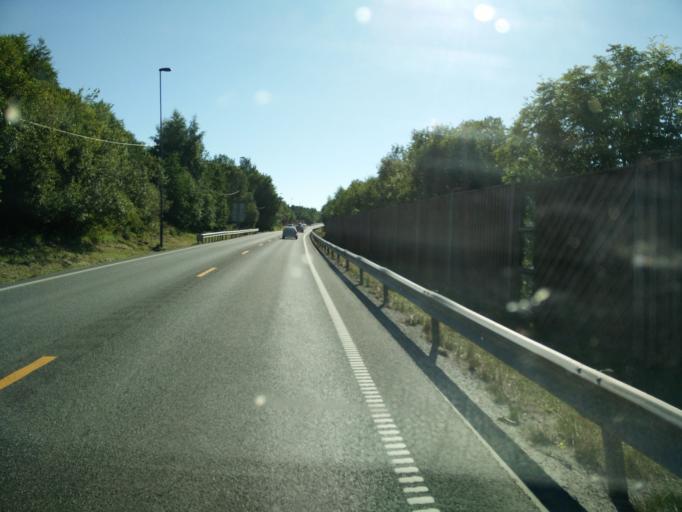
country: NO
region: Sor-Trondelag
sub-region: Orkdal
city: Orkanger
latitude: 63.3125
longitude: 9.8657
